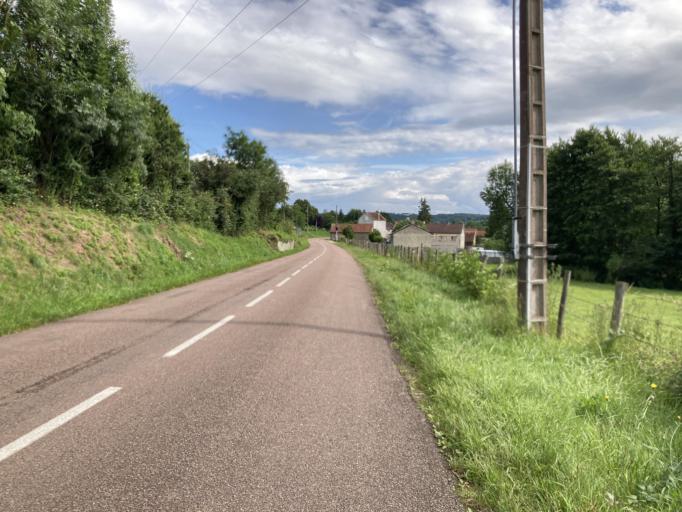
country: FR
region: Bourgogne
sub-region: Departement de la Cote-d'Or
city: Montbard
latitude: 47.6266
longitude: 4.3676
